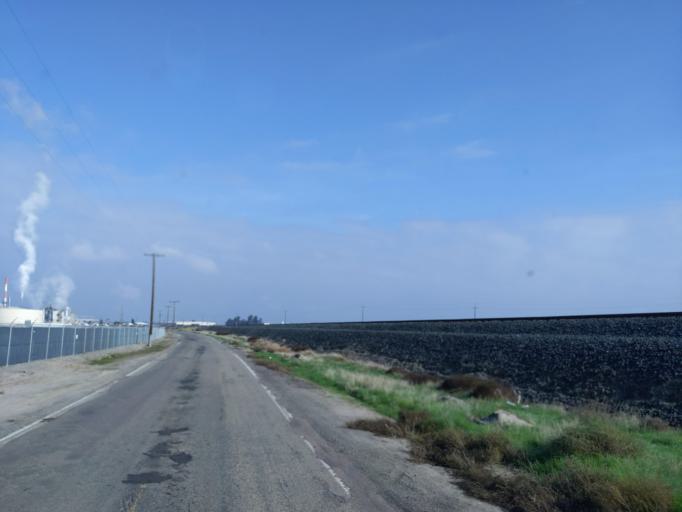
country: US
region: California
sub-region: San Joaquin County
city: Lathrop
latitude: 37.8009
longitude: -121.2773
